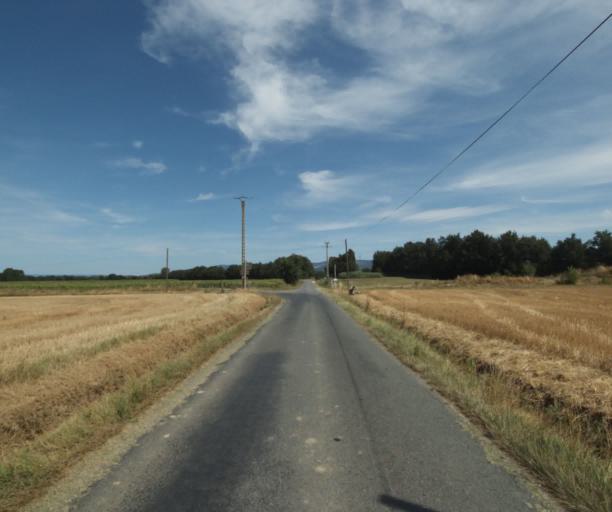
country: FR
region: Midi-Pyrenees
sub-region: Departement du Tarn
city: Puylaurens
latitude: 43.5165
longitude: 2.0193
